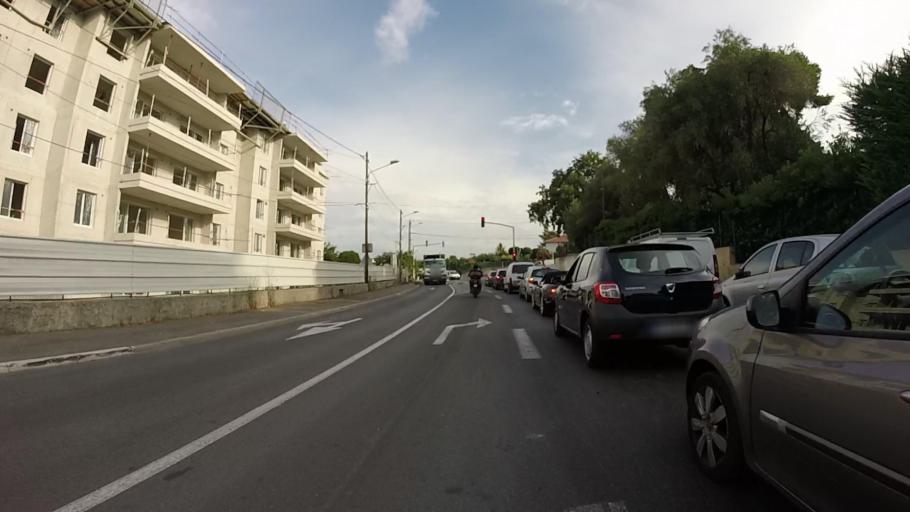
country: FR
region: Provence-Alpes-Cote d'Azur
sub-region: Departement des Alpes-Maritimes
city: Biot
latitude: 43.5957
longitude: 7.1063
